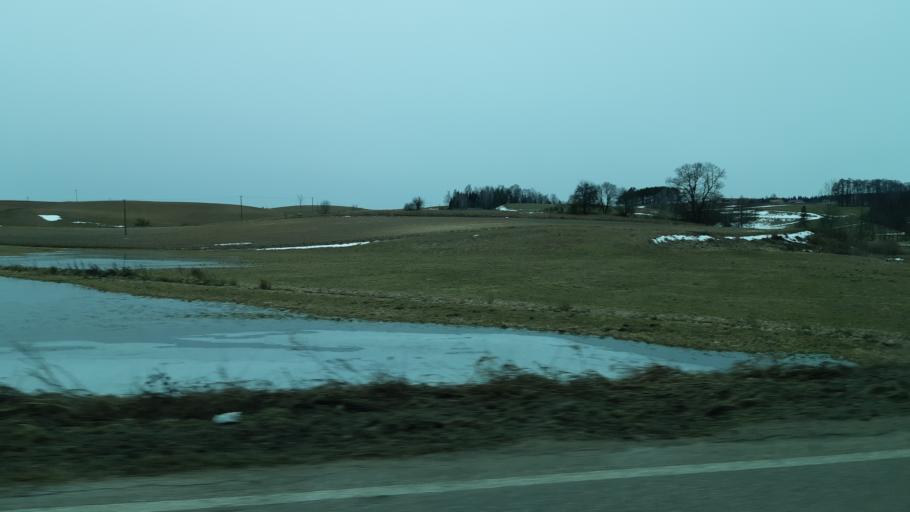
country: PL
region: Podlasie
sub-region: Suwalki
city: Suwalki
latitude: 54.3303
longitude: 22.9536
